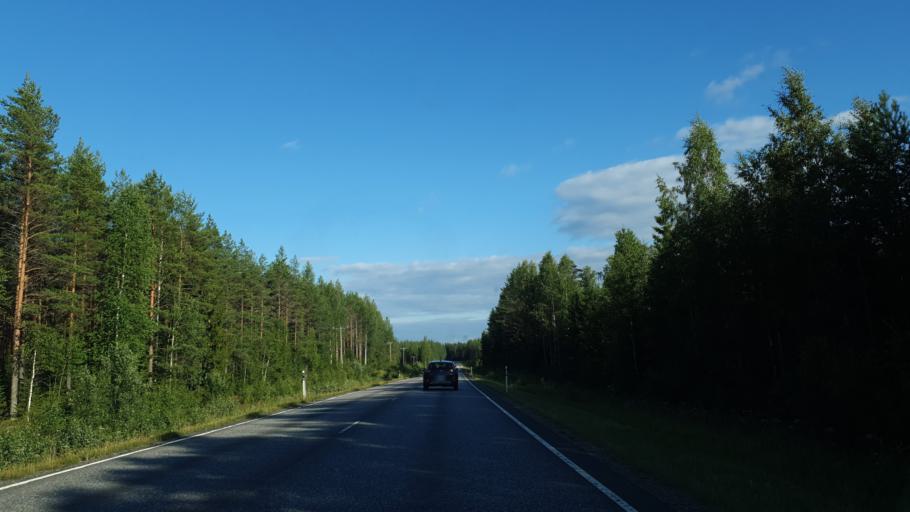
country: FI
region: North Karelia
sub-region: Joensuu
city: Outokumpu
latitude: 62.5282
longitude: 28.9901
